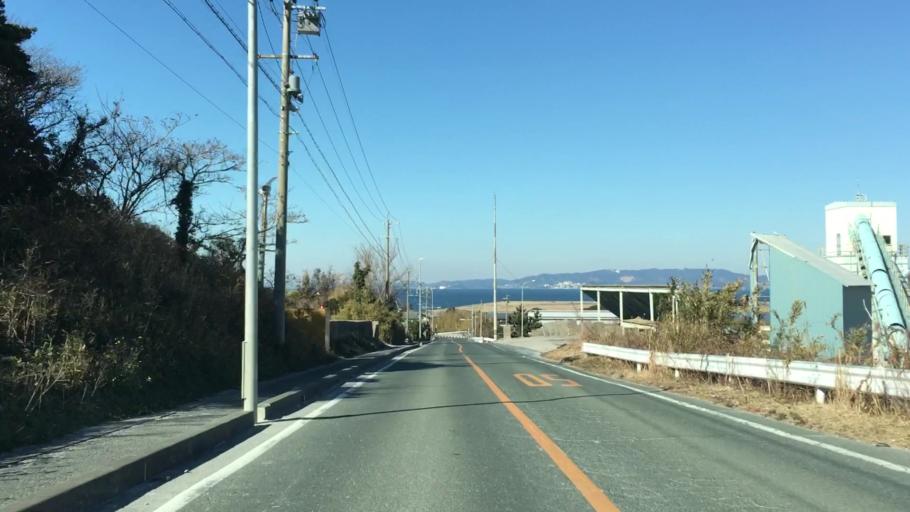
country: JP
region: Aichi
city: Tahara
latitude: 34.6846
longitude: 137.2482
